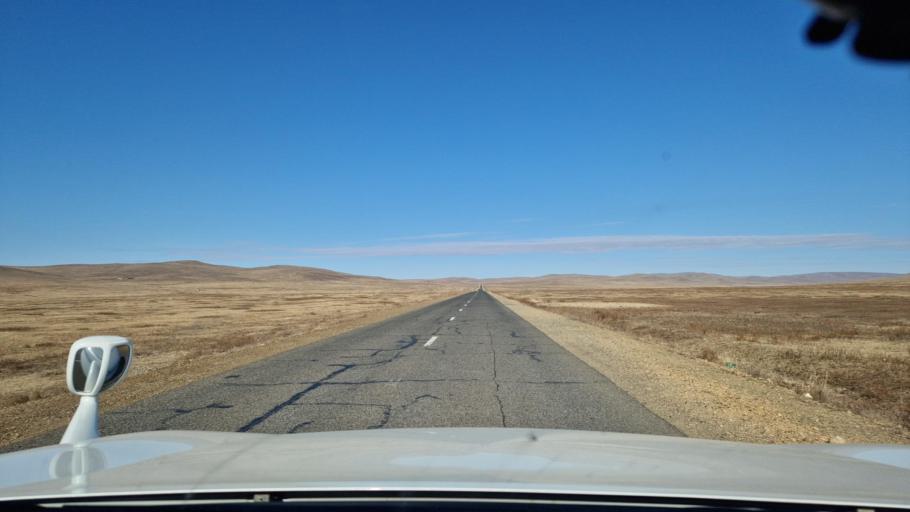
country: MN
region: Hentiy
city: Avraga
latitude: 47.5174
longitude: 109.4231
